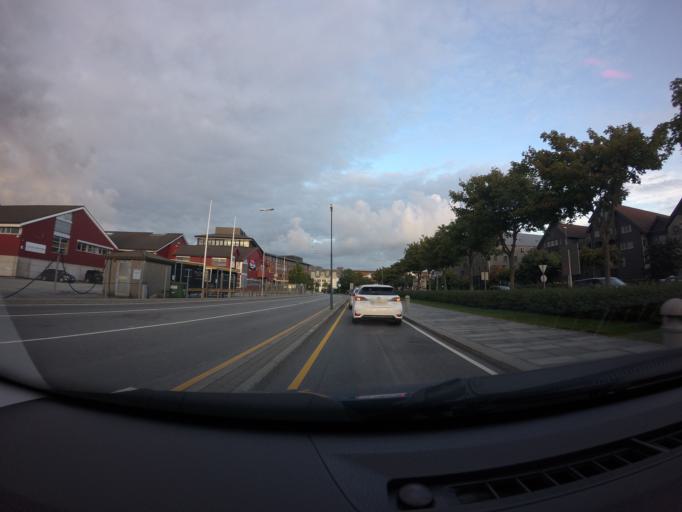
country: NO
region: Rogaland
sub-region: Stavanger
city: Stavanger
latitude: 58.9714
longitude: 5.7432
